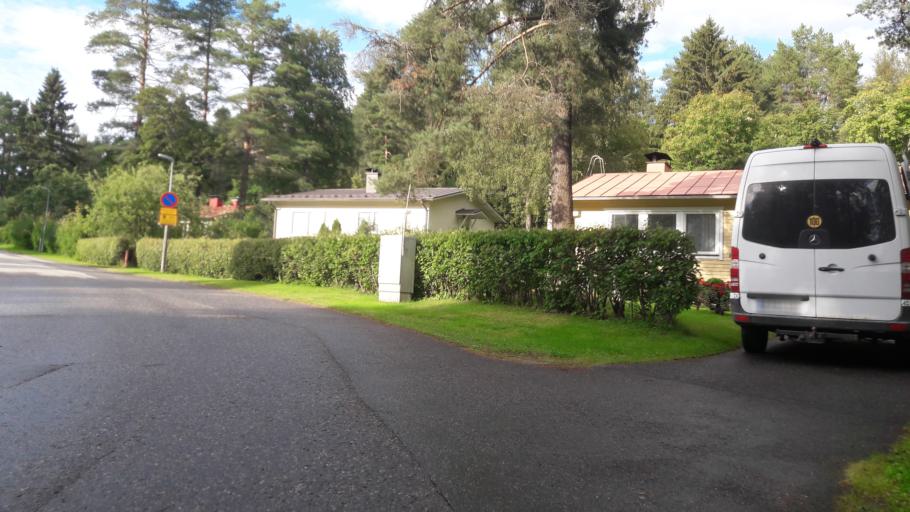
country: FI
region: North Karelia
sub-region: Joensuu
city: Joensuu
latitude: 62.5838
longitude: 29.7860
